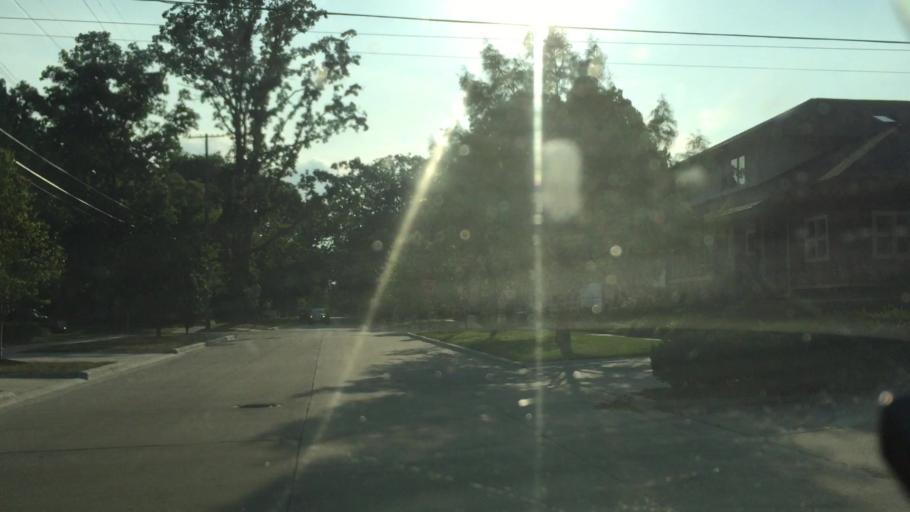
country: US
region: Michigan
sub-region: Oakland County
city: Beverly Hills
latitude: 42.5340
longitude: -83.2162
